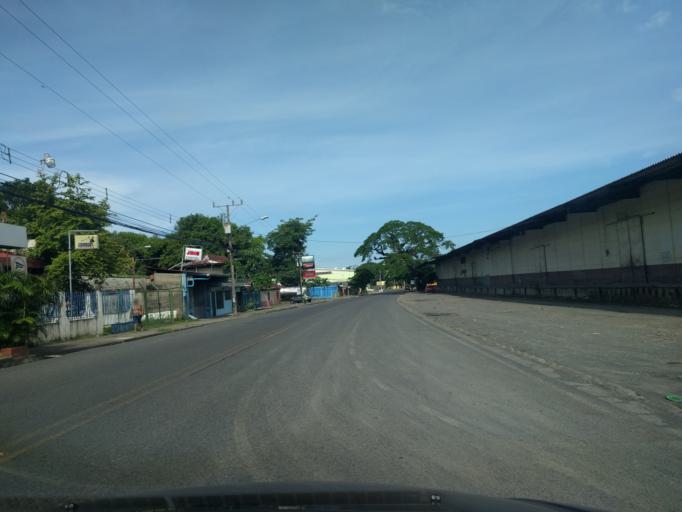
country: CR
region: Puntarenas
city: Esparza
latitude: 9.9898
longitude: -84.7106
